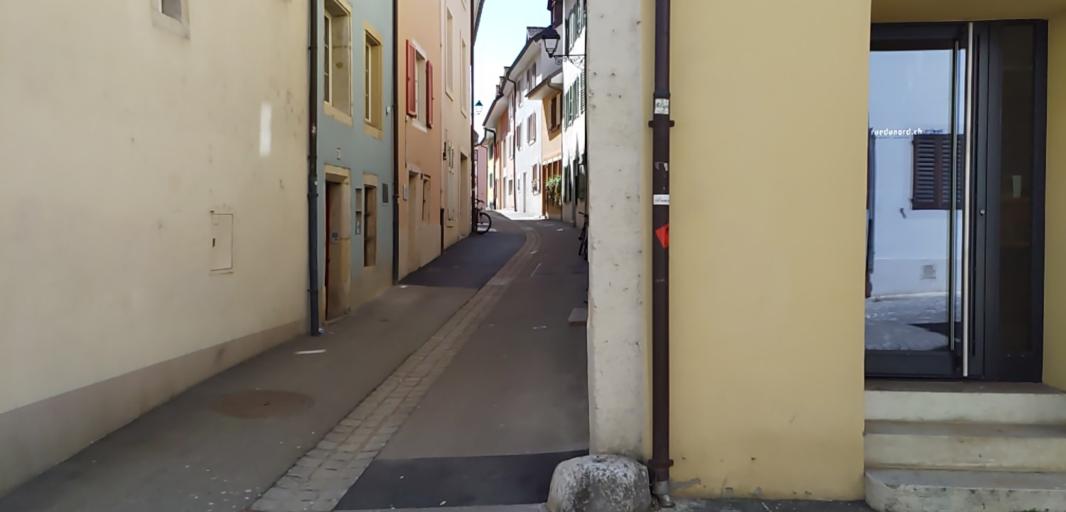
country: CH
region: Jura
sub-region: Delemont District
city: Delemont
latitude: 47.3665
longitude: 7.3433
